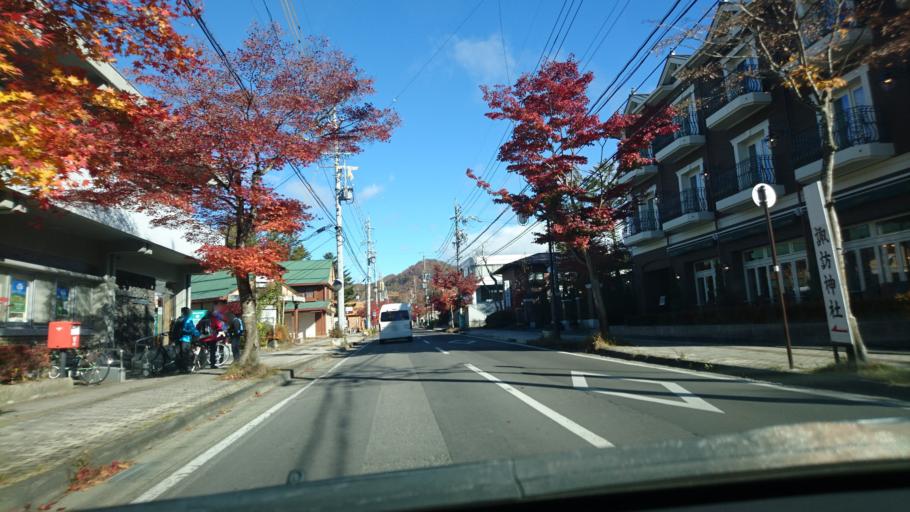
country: JP
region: Nagano
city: Saku
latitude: 36.3526
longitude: 138.6342
